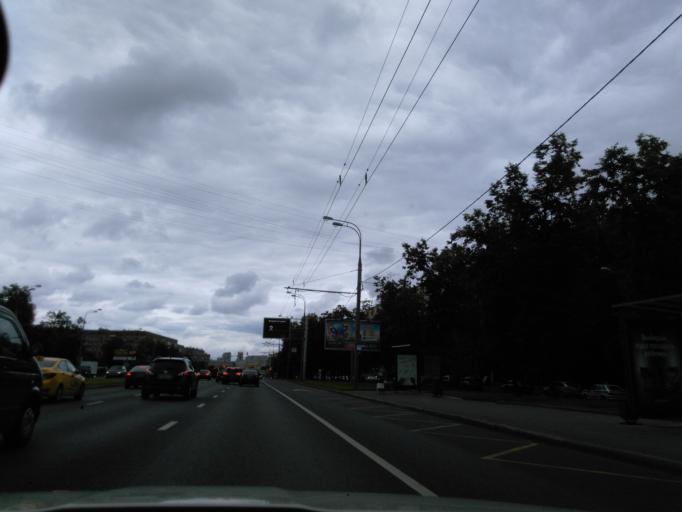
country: RU
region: Moskovskaya
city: Leninskiye Gory
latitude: 55.7023
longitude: 37.5708
